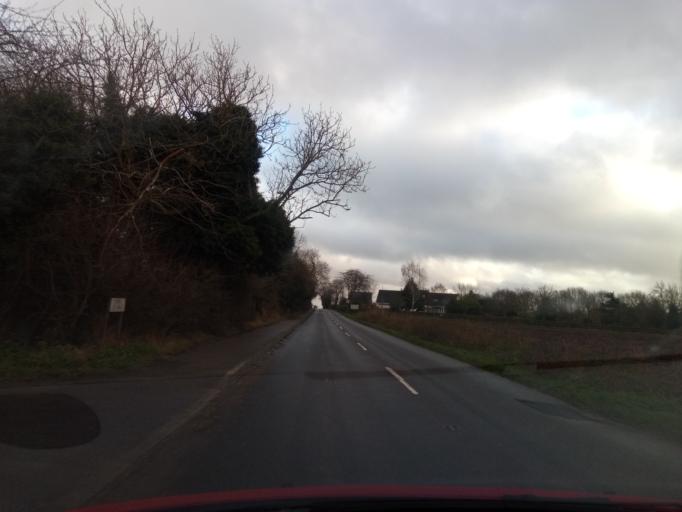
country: GB
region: England
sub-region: Derbyshire
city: Melbourne
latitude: 52.8490
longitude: -1.4139
